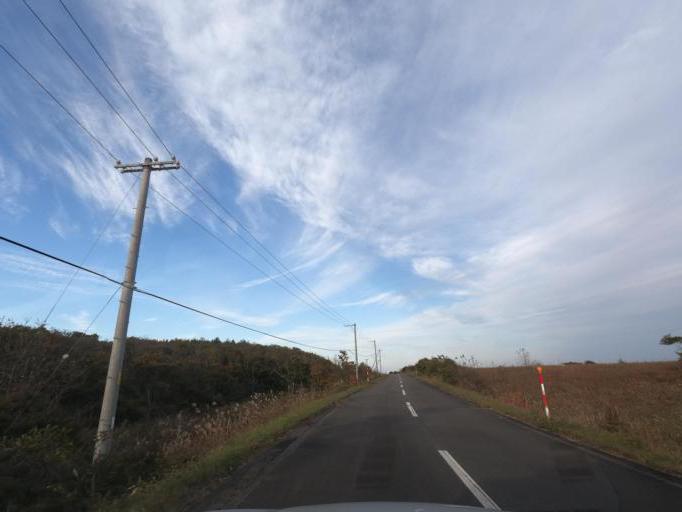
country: JP
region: Hokkaido
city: Obihiro
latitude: 42.5372
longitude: 143.4873
